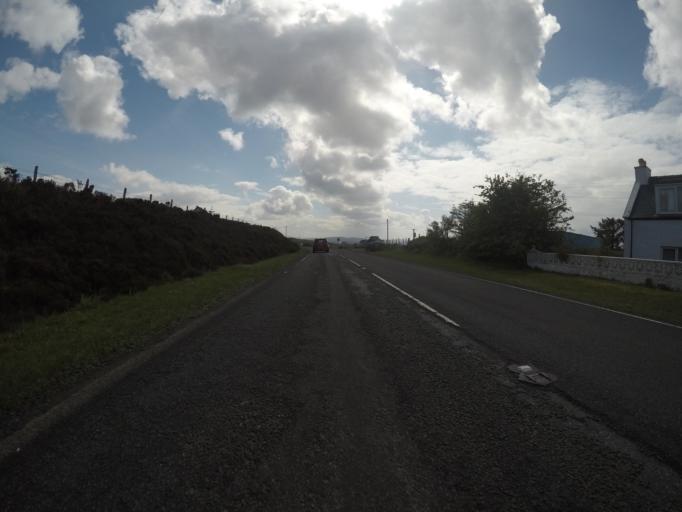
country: GB
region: Scotland
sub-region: Highland
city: Portree
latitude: 57.5664
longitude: -6.3648
